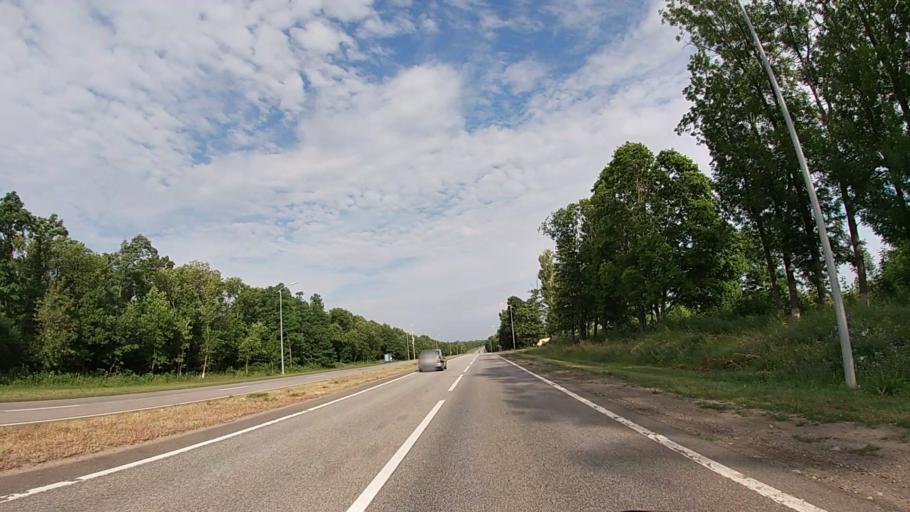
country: RU
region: Belgorod
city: Tomarovka
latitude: 50.6640
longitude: 36.3265
